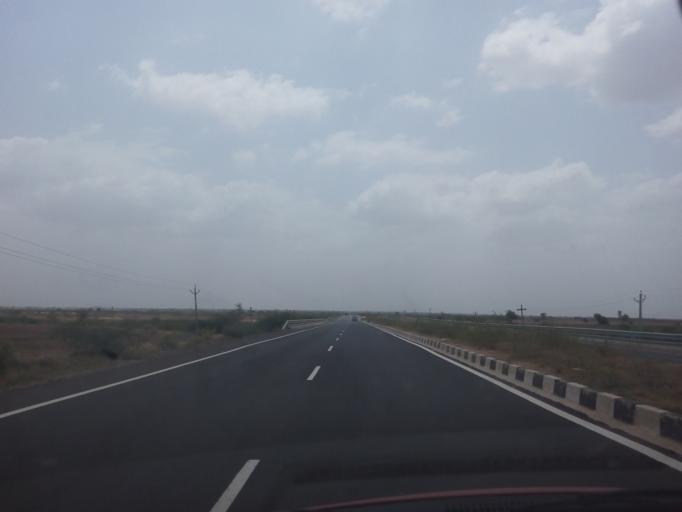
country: IN
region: Gujarat
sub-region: Surendranagar
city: Lakhtar
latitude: 23.0779
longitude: 71.8200
